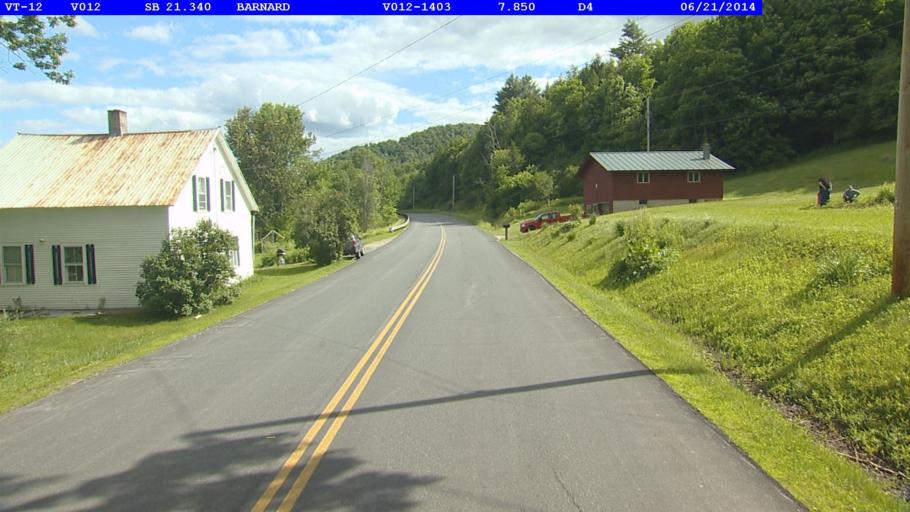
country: US
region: Vermont
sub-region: Orange County
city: Randolph
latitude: 43.7687
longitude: -72.6373
